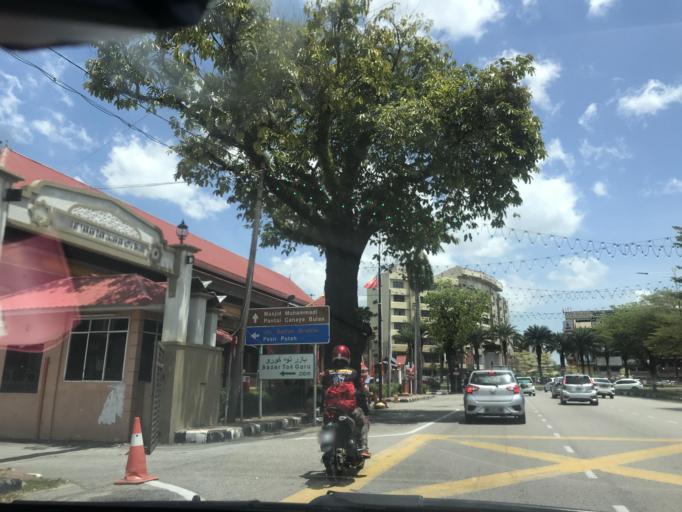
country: MY
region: Kelantan
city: Kota Bharu
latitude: 6.1252
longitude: 102.2387
